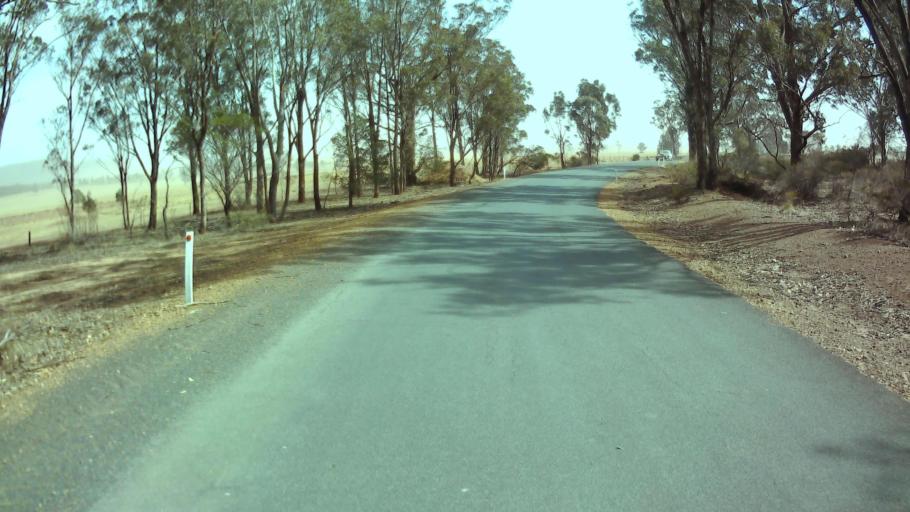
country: AU
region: New South Wales
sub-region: Weddin
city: Grenfell
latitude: -33.7743
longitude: 147.9864
